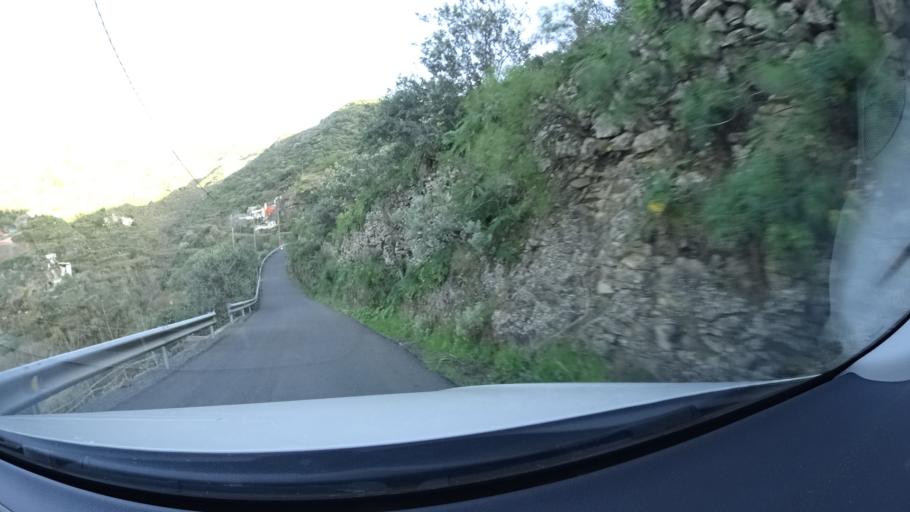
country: ES
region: Canary Islands
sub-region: Provincia de Las Palmas
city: Artenara
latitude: 28.0340
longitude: -15.6447
